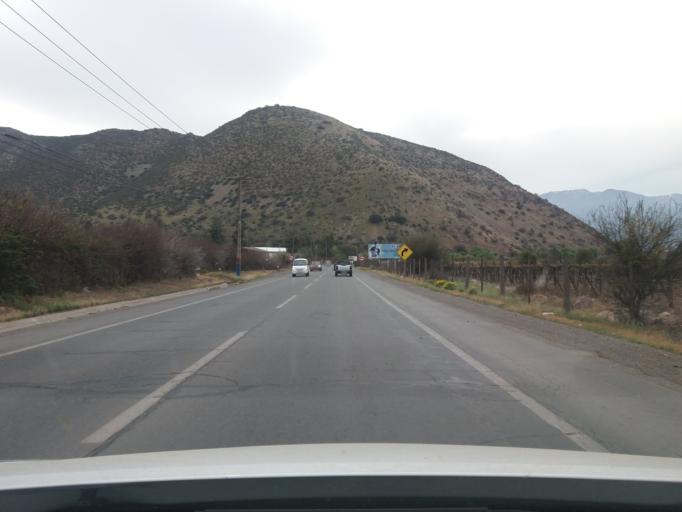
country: CL
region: Valparaiso
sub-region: Provincia de San Felipe
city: San Felipe
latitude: -32.7656
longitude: -70.7320
